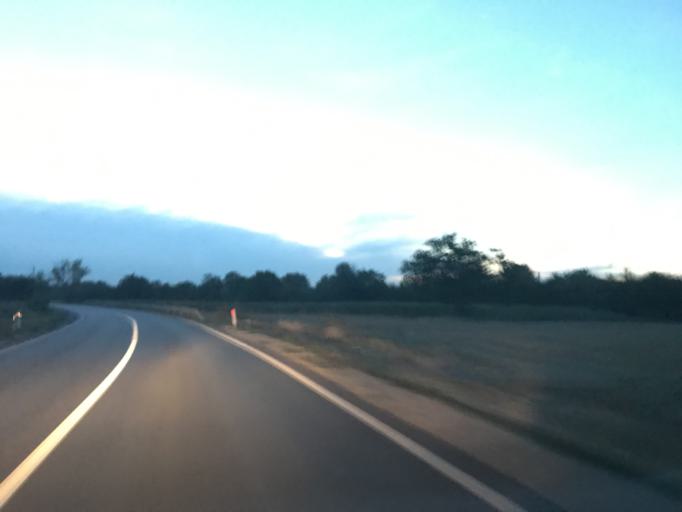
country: RS
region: Central Serbia
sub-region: Podunavski Okrug
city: Smederevo
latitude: 44.5840
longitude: 20.9828
